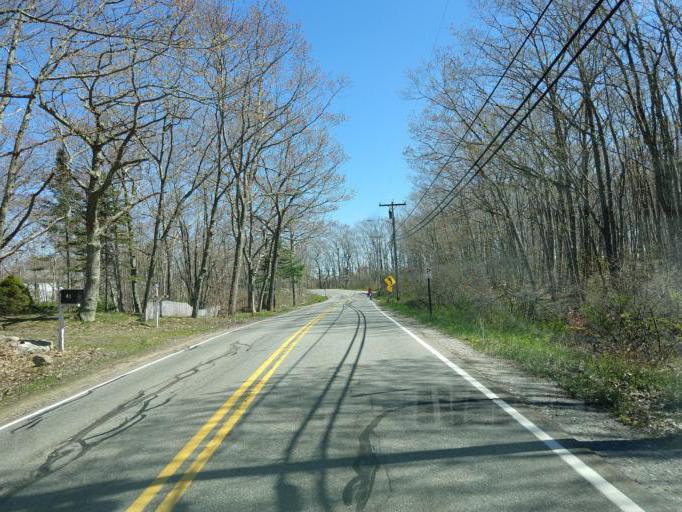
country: US
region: Maine
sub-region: York County
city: Old Orchard Beach
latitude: 43.4383
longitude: -70.3729
